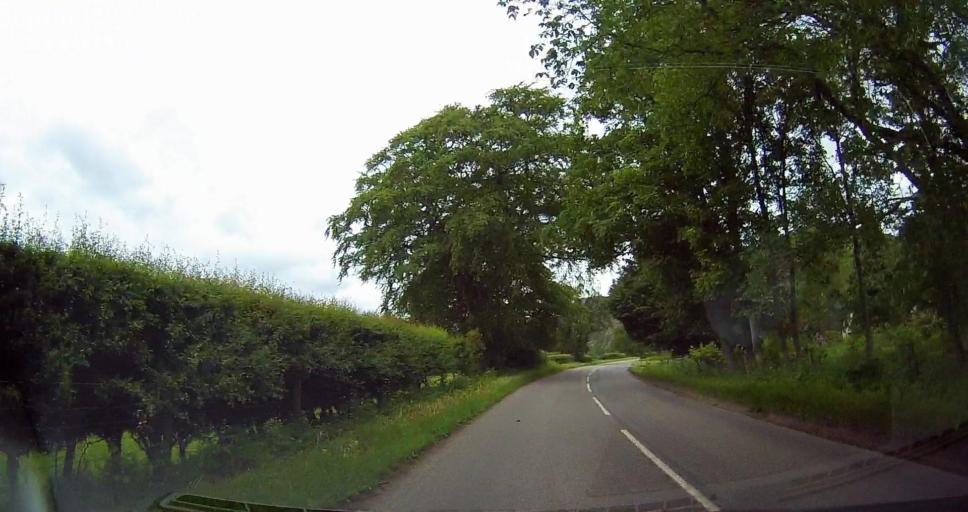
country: GB
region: Scotland
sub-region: Highland
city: Dornoch
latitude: 57.9774
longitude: -4.1085
